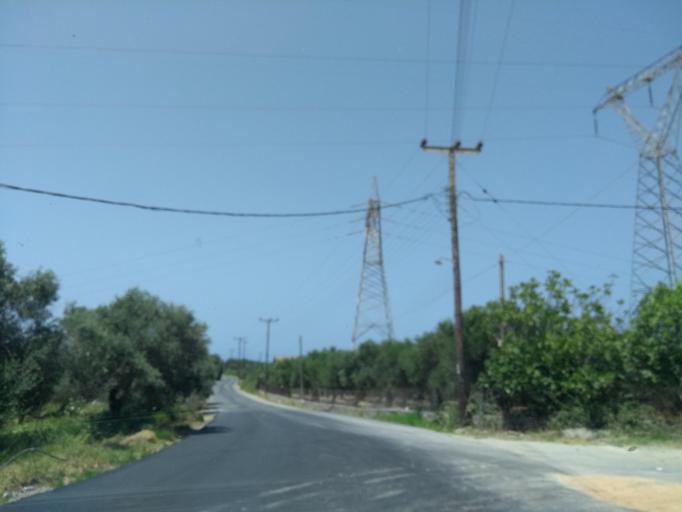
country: GR
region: Crete
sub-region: Nomos Chanias
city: Georgioupolis
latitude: 35.3384
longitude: 24.3020
